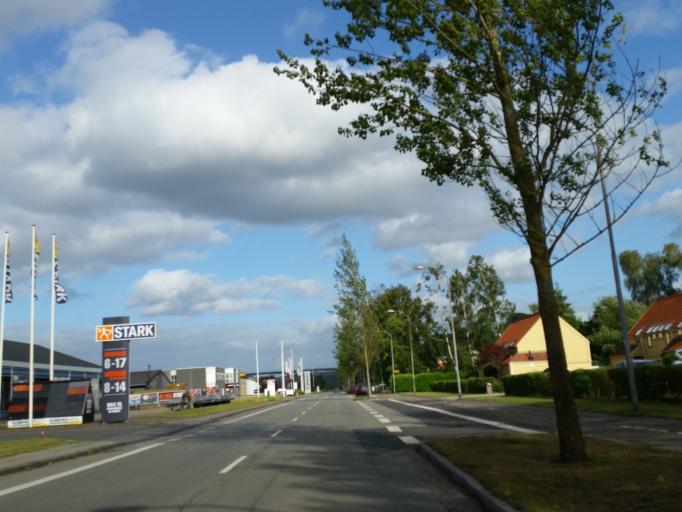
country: DK
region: South Denmark
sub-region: Vejle Kommune
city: Vejle
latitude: 55.7011
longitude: 9.5470
